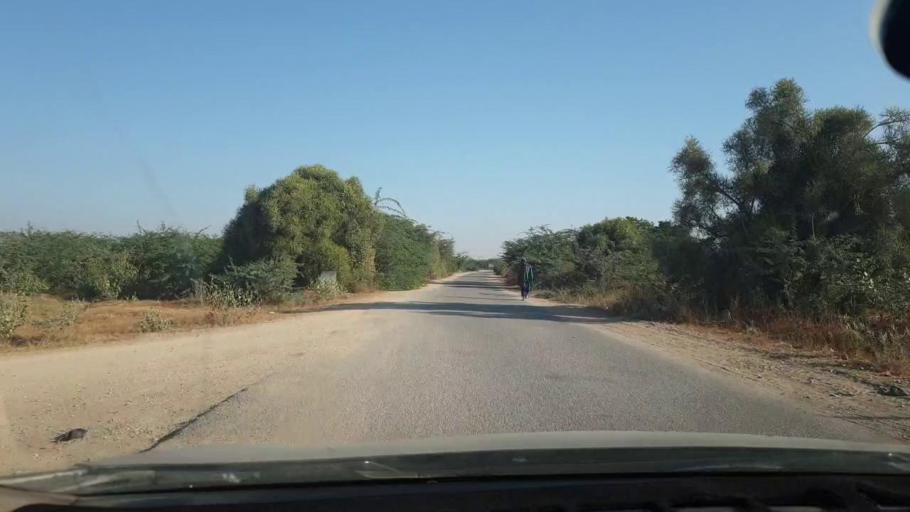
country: PK
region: Sindh
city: Malir Cantonment
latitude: 25.1738
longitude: 67.2024
